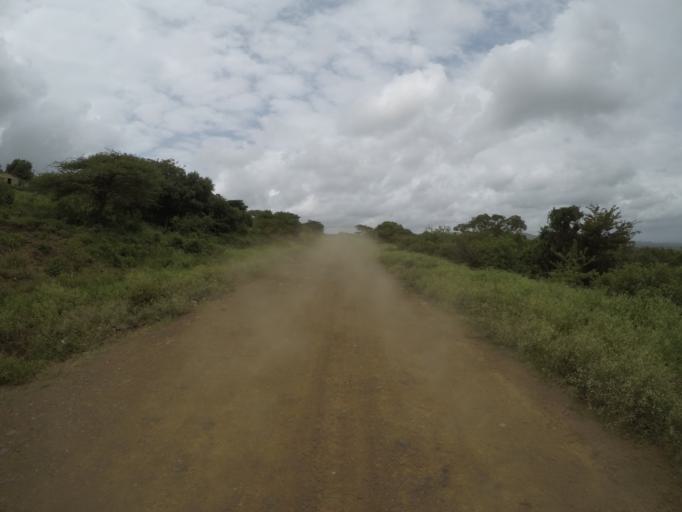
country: ZA
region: KwaZulu-Natal
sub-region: uThungulu District Municipality
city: Empangeni
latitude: -28.6057
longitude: 31.8944
